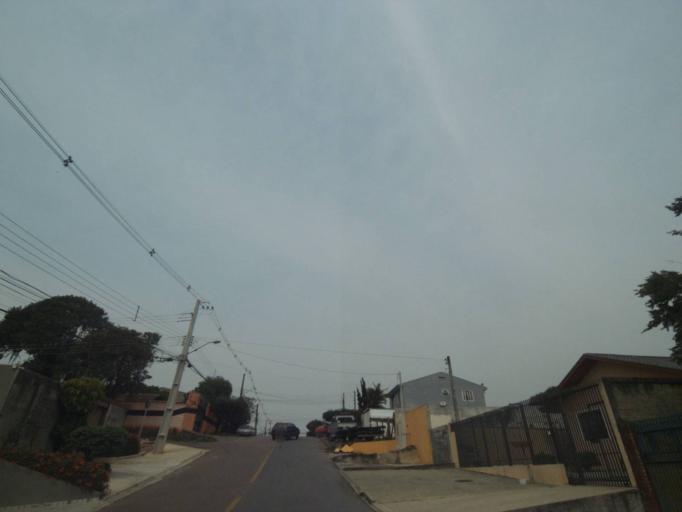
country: BR
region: Parana
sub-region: Sao Jose Dos Pinhais
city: Sao Jose dos Pinhais
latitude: -25.5200
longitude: -49.2876
